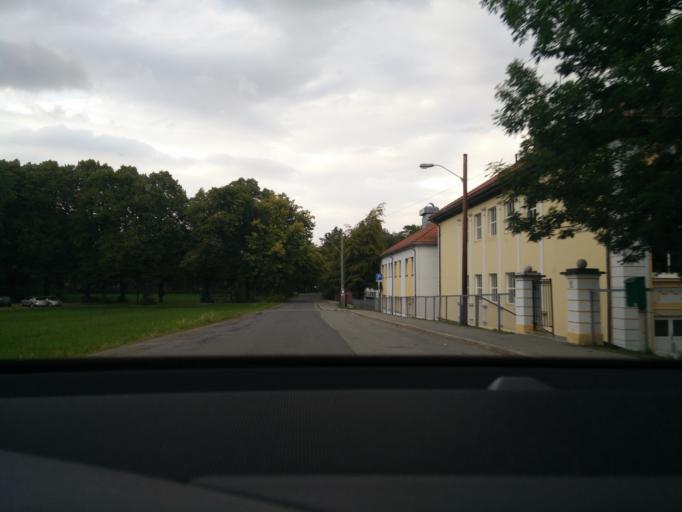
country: NO
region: Oslo
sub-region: Oslo
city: Sjolyststranda
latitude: 59.9048
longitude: 10.6760
